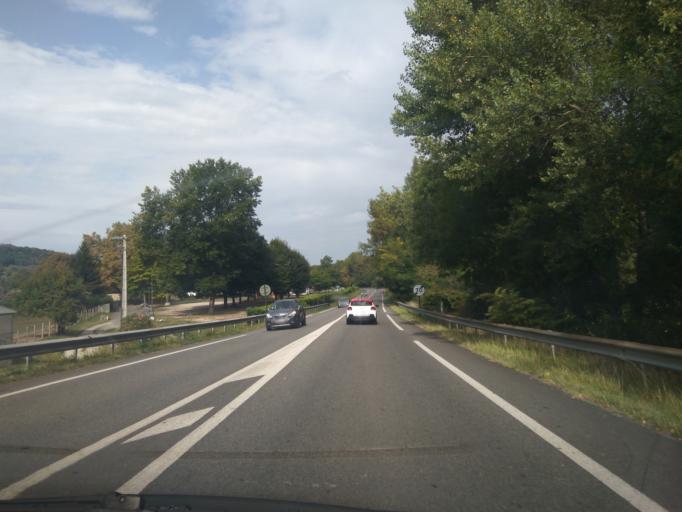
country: FR
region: Aquitaine
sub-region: Departement des Pyrenees-Atlantiques
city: Artiguelouve
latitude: 43.3050
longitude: -0.4394
